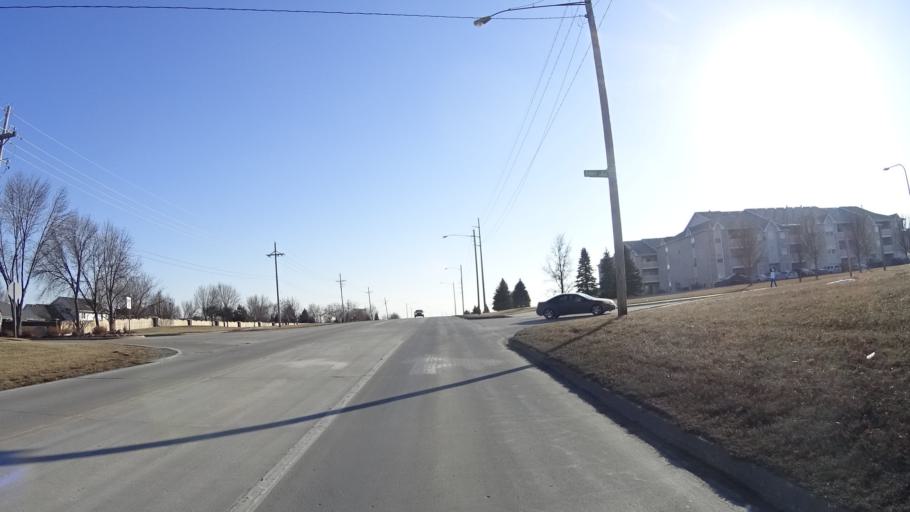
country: US
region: Nebraska
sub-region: Douglas County
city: Bennington
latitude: 41.2993
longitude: -96.1389
